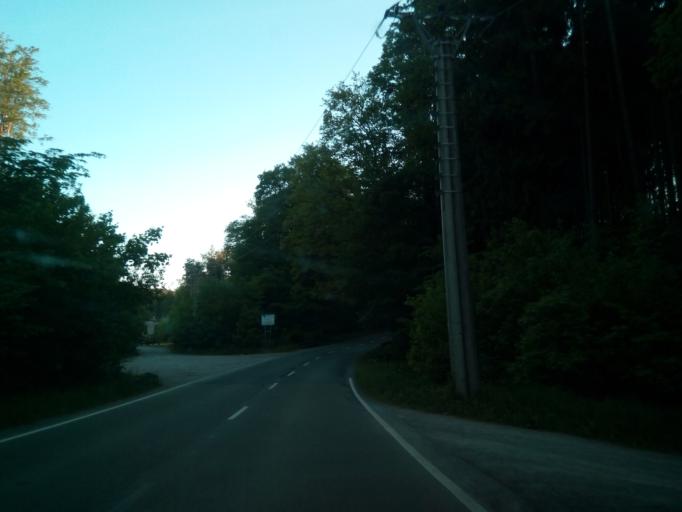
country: CZ
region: South Moravian
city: Bilovice nad Svitavou
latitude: 49.2703
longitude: 16.7403
